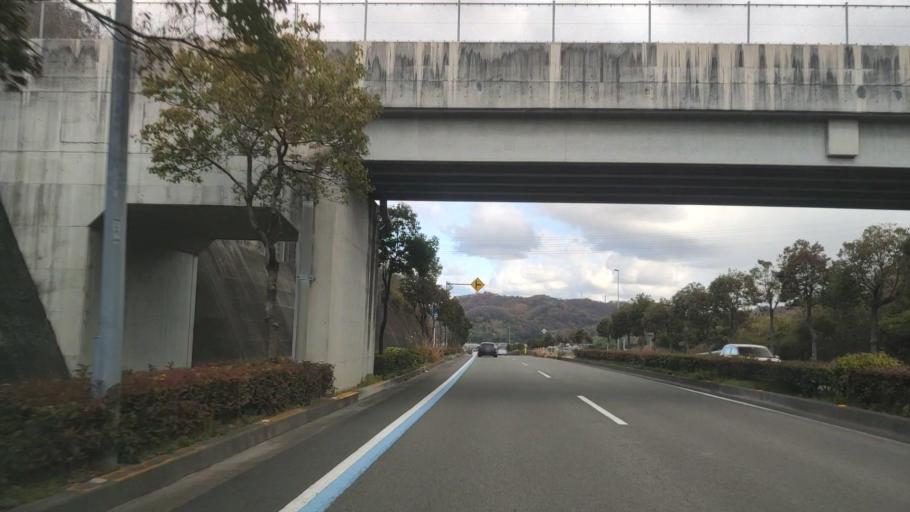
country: JP
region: Ehime
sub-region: Shikoku-chuo Shi
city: Matsuyama
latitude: 33.8910
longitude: 132.7572
